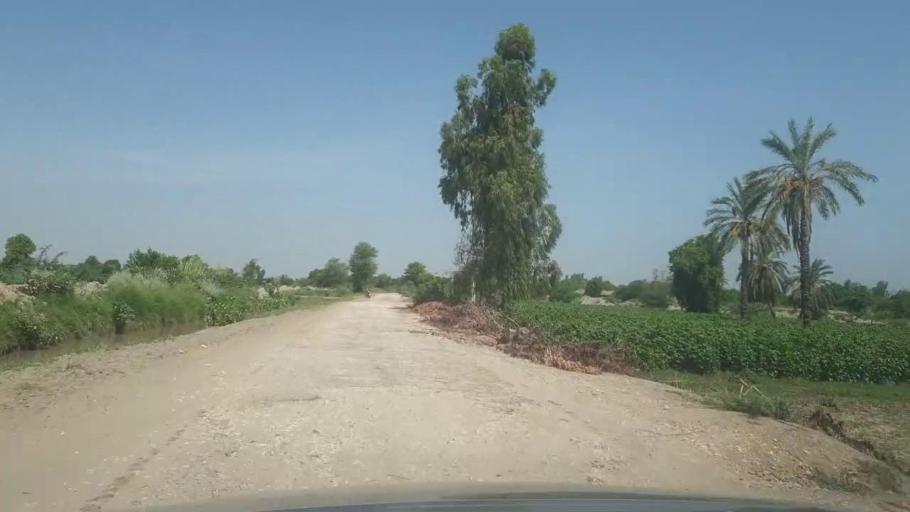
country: PK
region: Sindh
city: Khairpur
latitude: 27.4013
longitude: 69.0379
